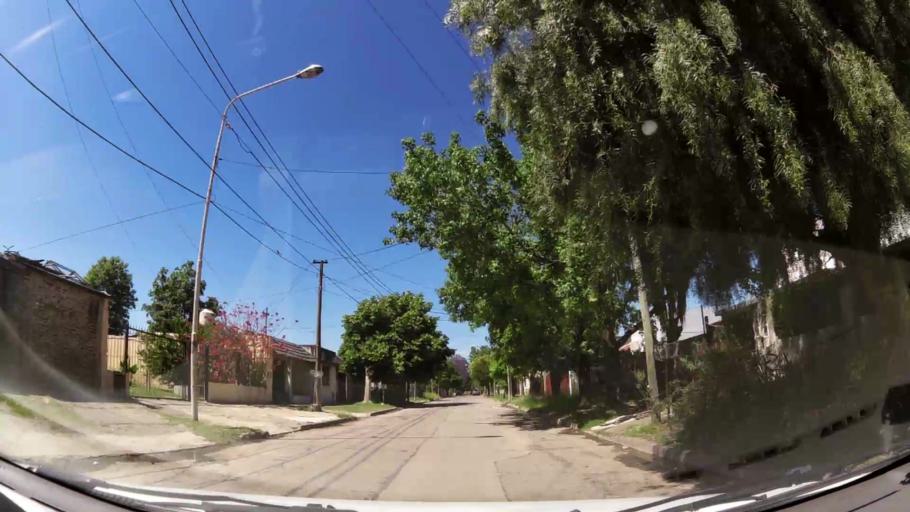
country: AR
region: Buenos Aires
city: Ituzaingo
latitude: -34.6775
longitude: -58.6590
